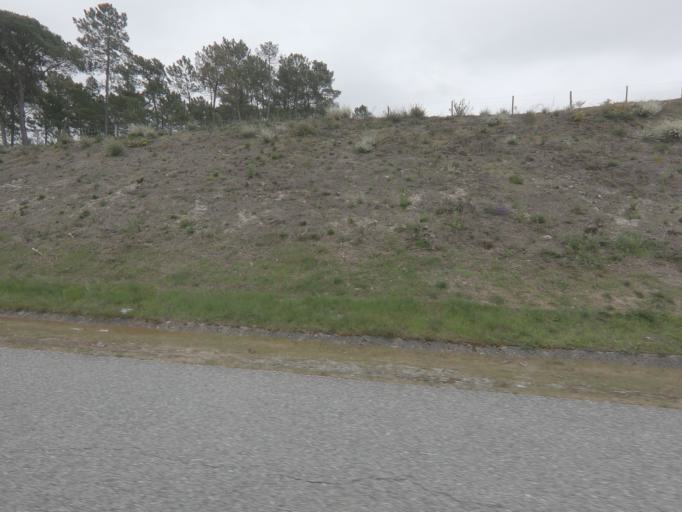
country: PT
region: Viseu
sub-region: Viseu
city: Viseu
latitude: 40.6269
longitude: -7.9047
